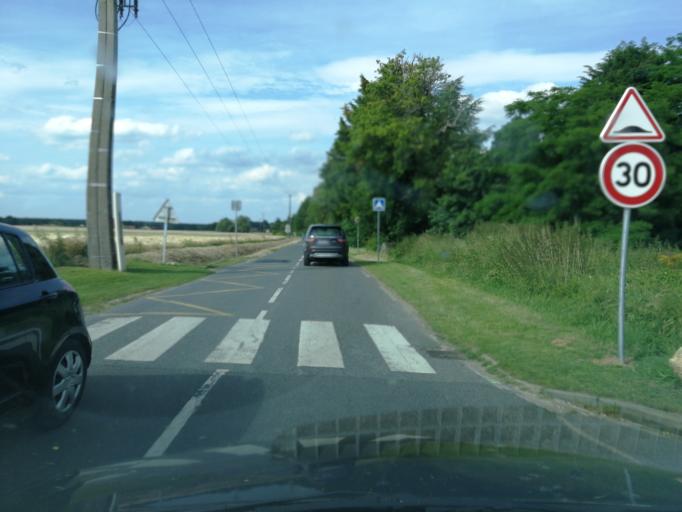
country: FR
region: Ile-de-France
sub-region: Departement de l'Essonne
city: Gometz-la-Ville
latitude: 48.6818
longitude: 2.1018
